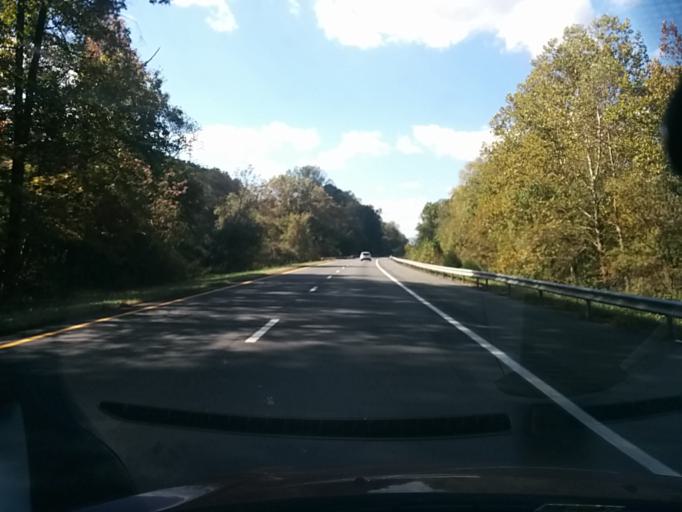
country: US
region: Virginia
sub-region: Albemarle County
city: Crozet
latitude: 38.0307
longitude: -78.6583
